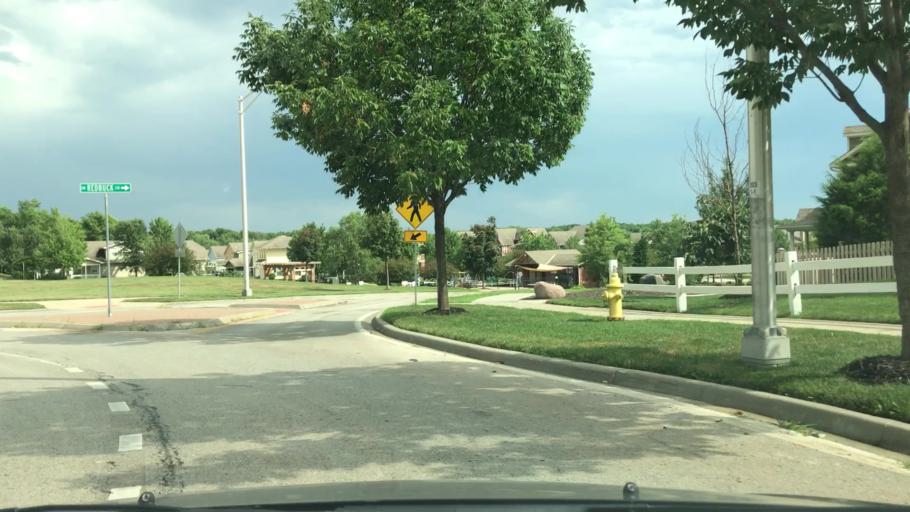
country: US
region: Missouri
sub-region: Jackson County
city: Lees Summit
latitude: 38.9057
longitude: -94.4474
